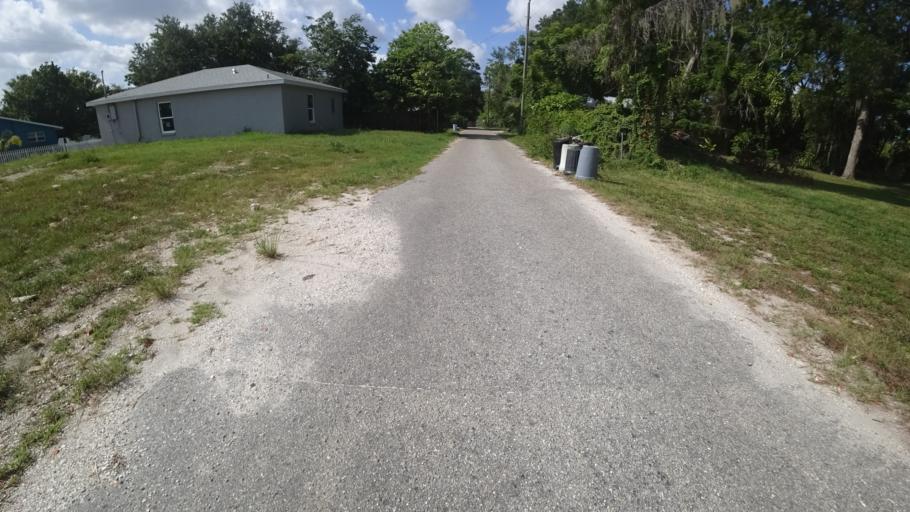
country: US
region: Florida
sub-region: Manatee County
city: Samoset
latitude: 27.4466
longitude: -82.5365
